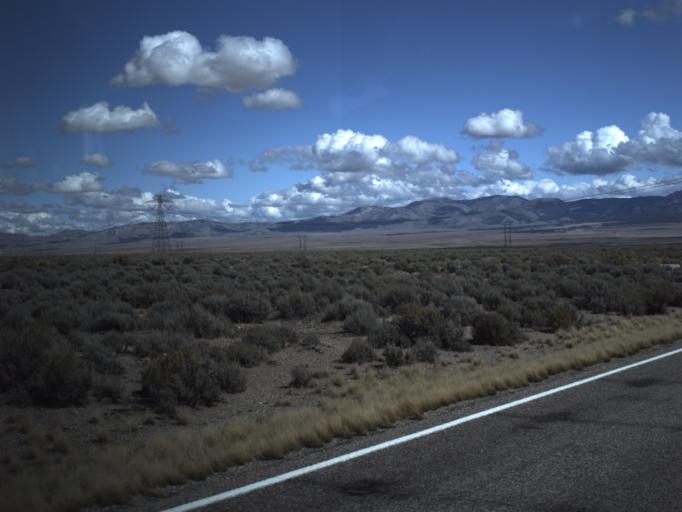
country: US
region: Utah
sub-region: Beaver County
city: Milford
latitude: 38.4120
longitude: -113.0693
